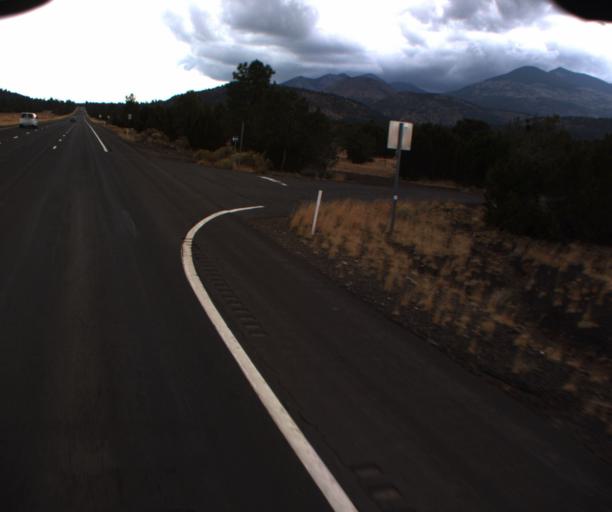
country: US
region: Arizona
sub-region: Coconino County
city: Flagstaff
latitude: 35.4054
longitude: -111.5750
